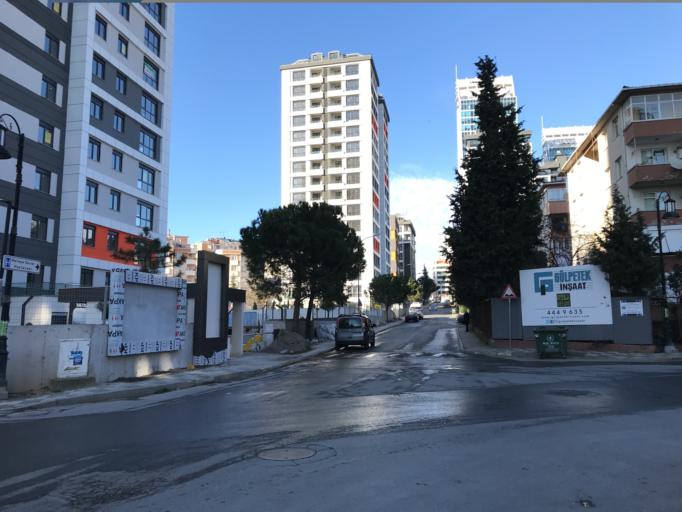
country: TR
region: Istanbul
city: Maltepe
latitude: 40.9334
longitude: 29.1329
